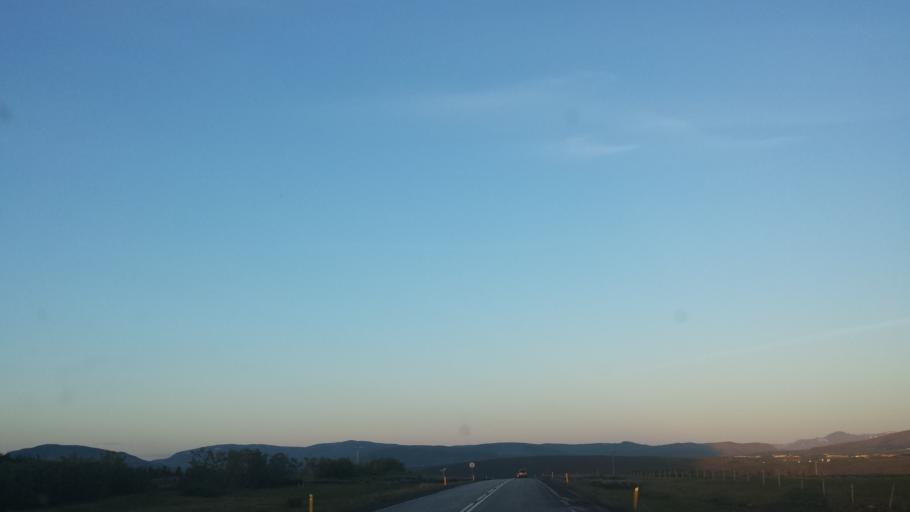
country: IS
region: Capital Region
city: Mosfellsbaer
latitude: 64.2090
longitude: -21.7641
